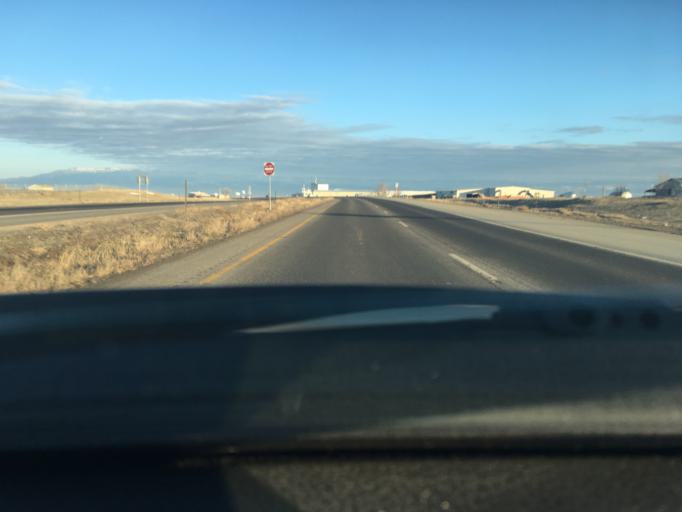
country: US
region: Colorado
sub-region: Montrose County
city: Olathe
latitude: 38.6055
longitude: -107.9734
